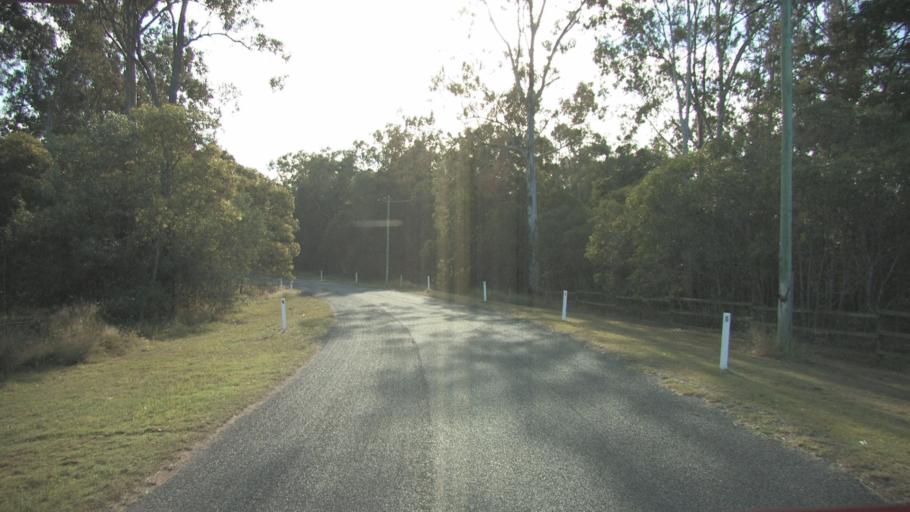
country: AU
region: Queensland
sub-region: Logan
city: North Maclean
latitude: -27.7571
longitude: 153.0062
